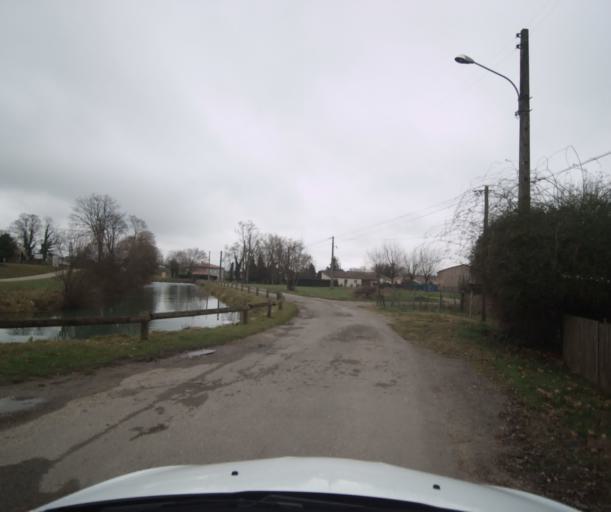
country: FR
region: Midi-Pyrenees
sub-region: Departement du Tarn-et-Garonne
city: Castelsarrasin
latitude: 44.0514
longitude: 1.1061
